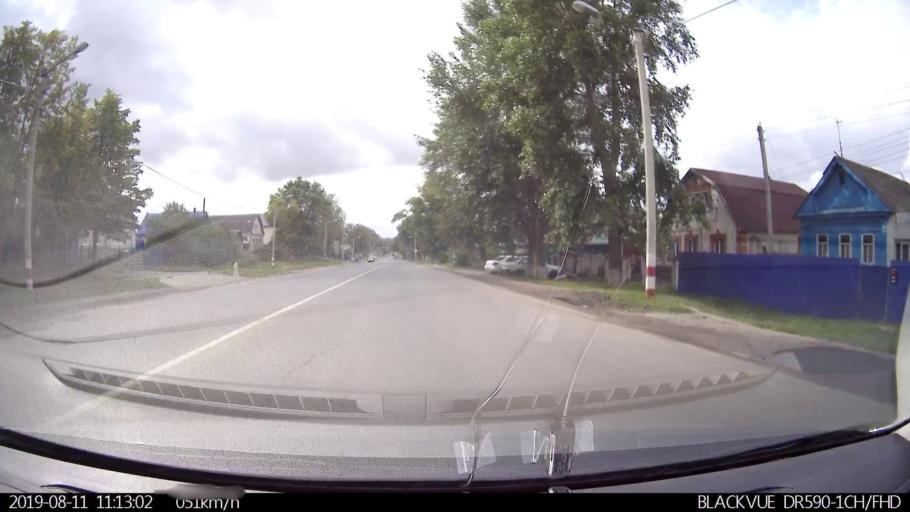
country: RU
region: Ulyanovsk
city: Novoul'yanovsk
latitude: 54.2196
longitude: 48.2984
